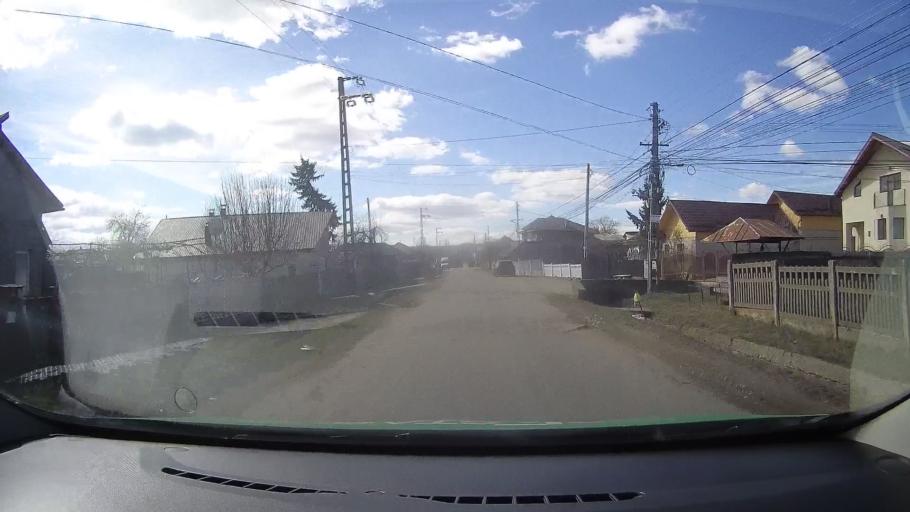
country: RO
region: Dambovita
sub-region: Comuna Doicesti
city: Doicesti
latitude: 44.9918
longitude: 25.4007
